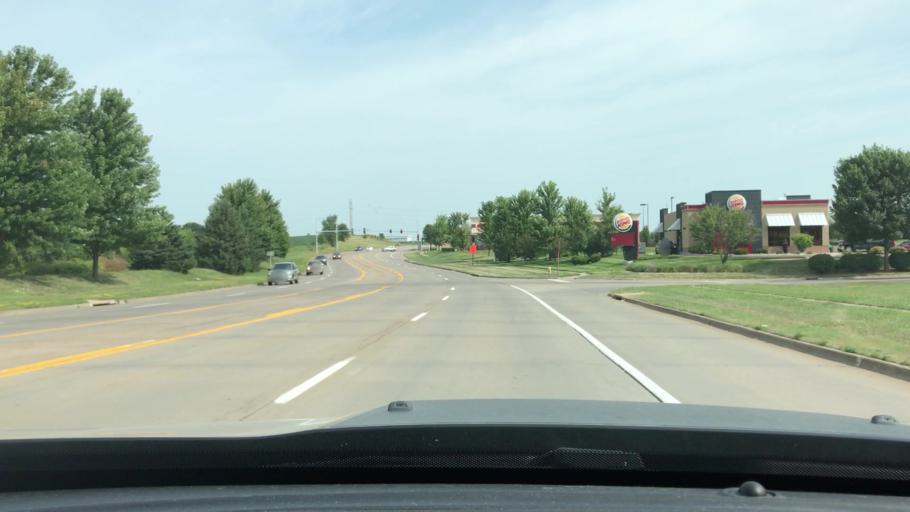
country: US
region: Iowa
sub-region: Scott County
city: Bettendorf
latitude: 41.5778
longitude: -90.5286
